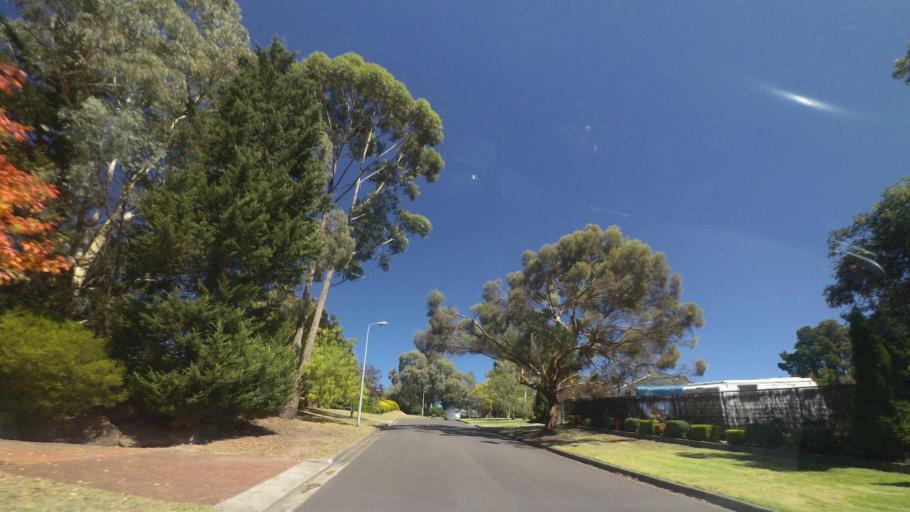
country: AU
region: Victoria
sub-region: Manningham
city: Donvale
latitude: -37.7863
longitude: 145.1882
